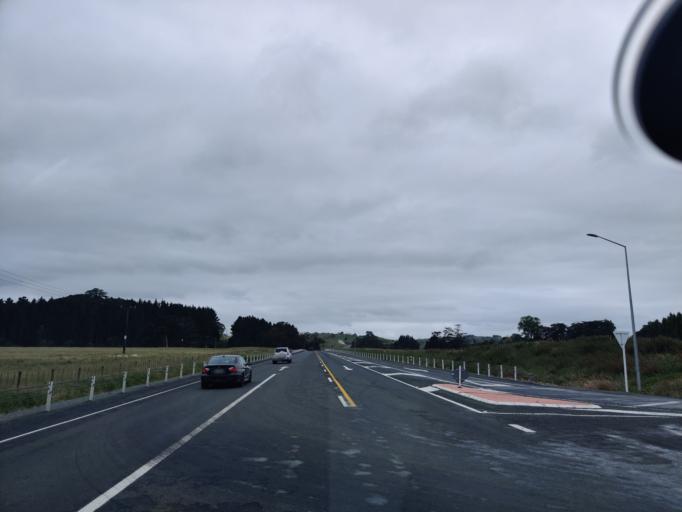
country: NZ
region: Northland
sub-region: Whangarei
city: Ruakaka
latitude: -36.1236
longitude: 174.1794
